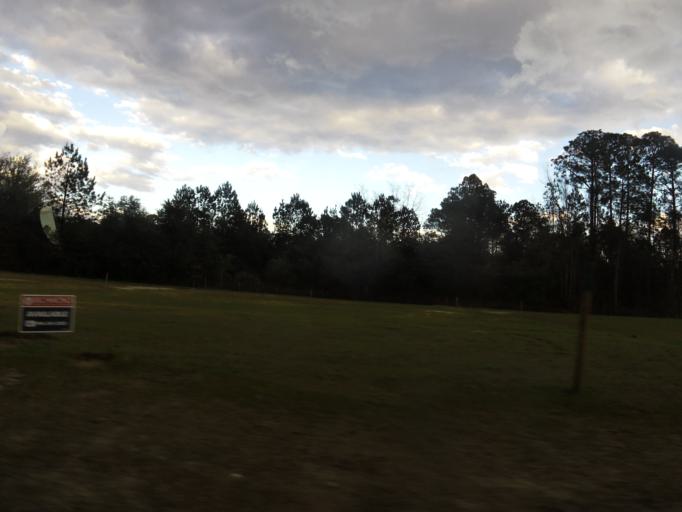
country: US
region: Florida
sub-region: Saint Johns County
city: Fruit Cove
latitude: 30.1743
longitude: -81.5766
